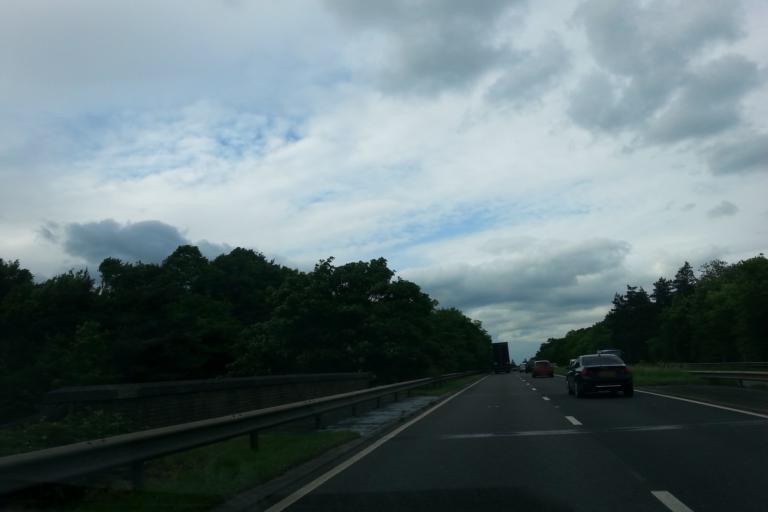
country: GB
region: England
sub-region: Leicestershire
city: Queniborough
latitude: 52.7217
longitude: -1.0754
